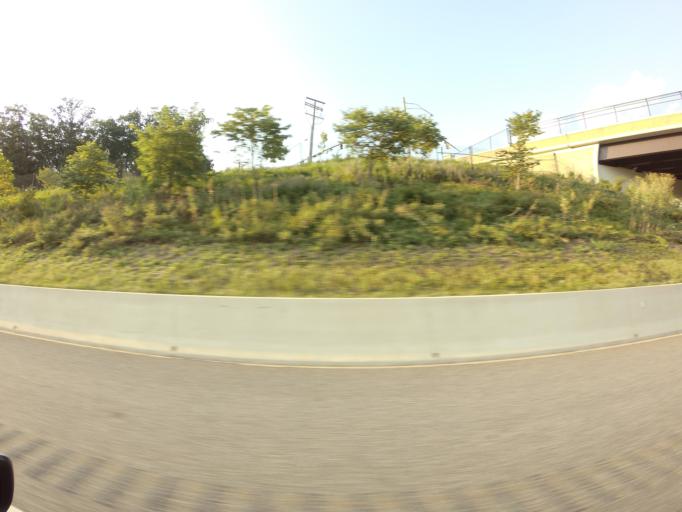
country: US
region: Maryland
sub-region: Prince George's County
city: Calverton
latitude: 39.0741
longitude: -76.9405
